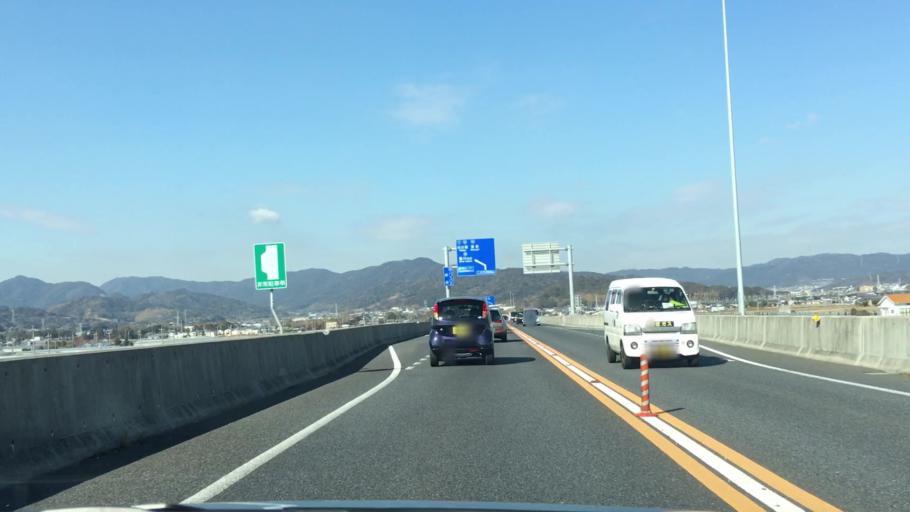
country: JP
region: Aichi
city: Kozakai-cho
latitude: 34.8132
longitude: 137.3332
